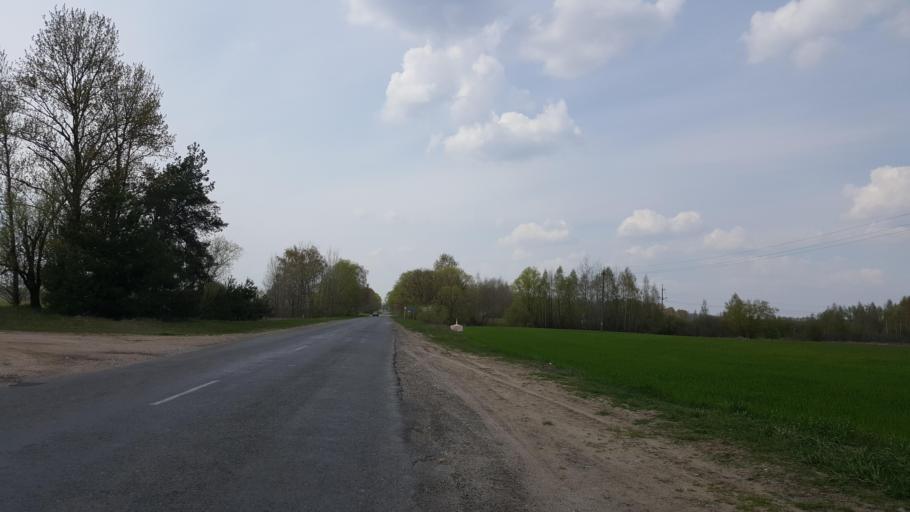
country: BY
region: Brest
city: Zhabinka
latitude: 52.2064
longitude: 23.9895
